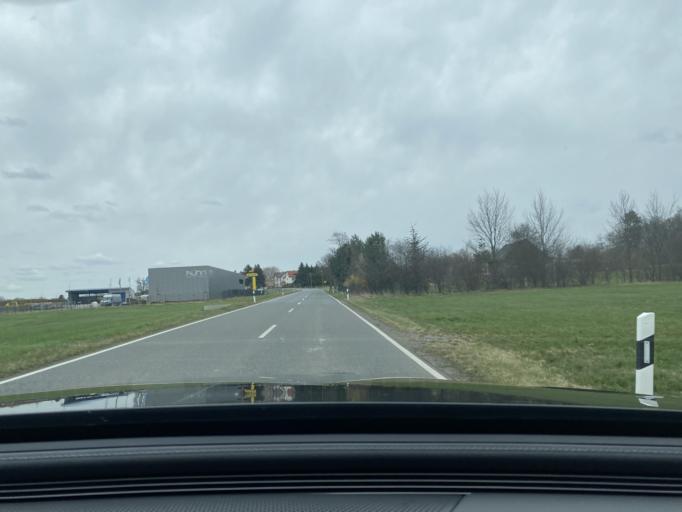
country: DE
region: Saxony
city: Durrrohrsdorf
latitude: 51.0251
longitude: 14.0161
